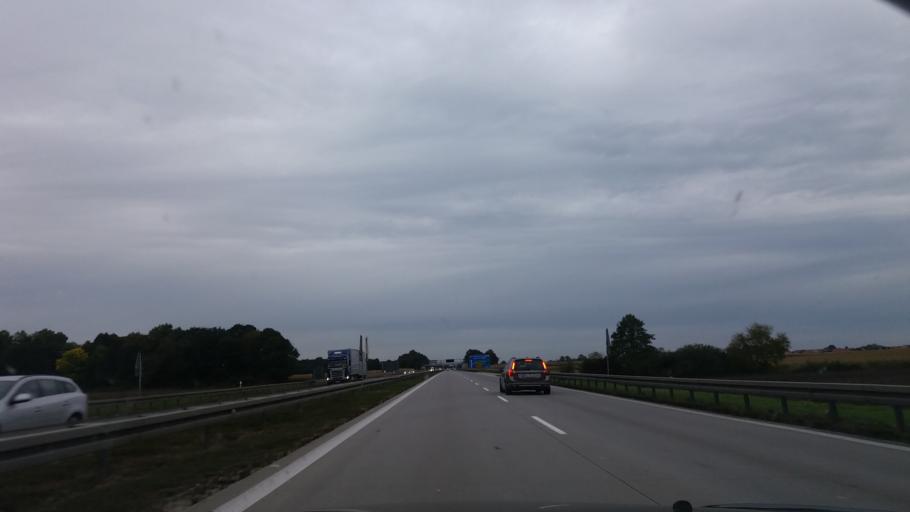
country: PL
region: Lower Silesian Voivodeship
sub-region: Powiat sredzki
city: Udanin
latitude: 51.0769
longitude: 16.4473
